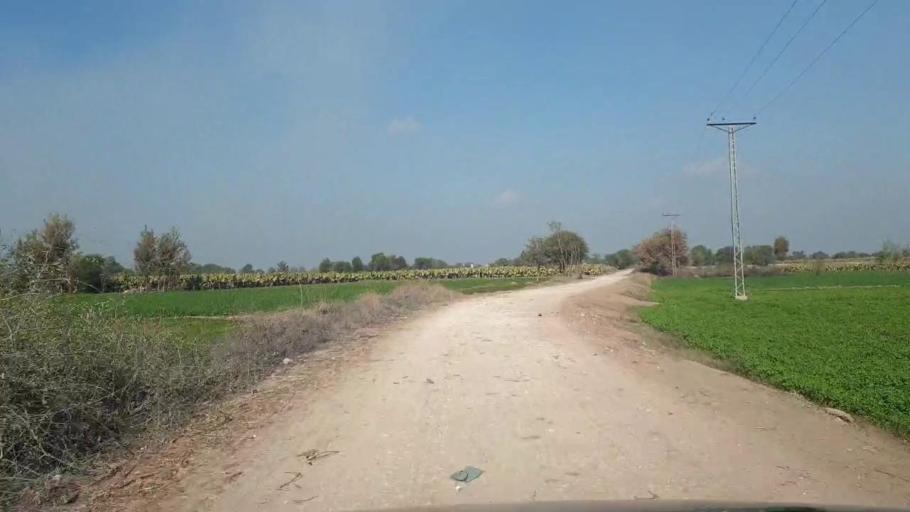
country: PK
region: Sindh
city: Shahdadpur
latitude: 25.9269
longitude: 68.5858
